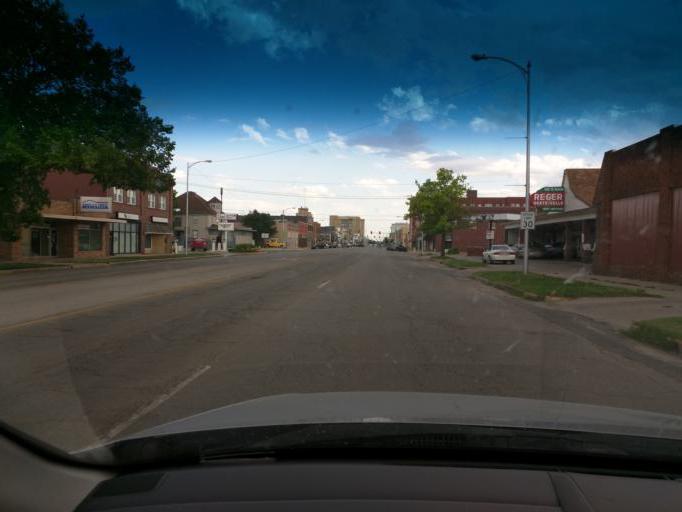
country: US
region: Kansas
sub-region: Reno County
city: Hutchinson
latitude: 38.0605
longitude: -97.9319
